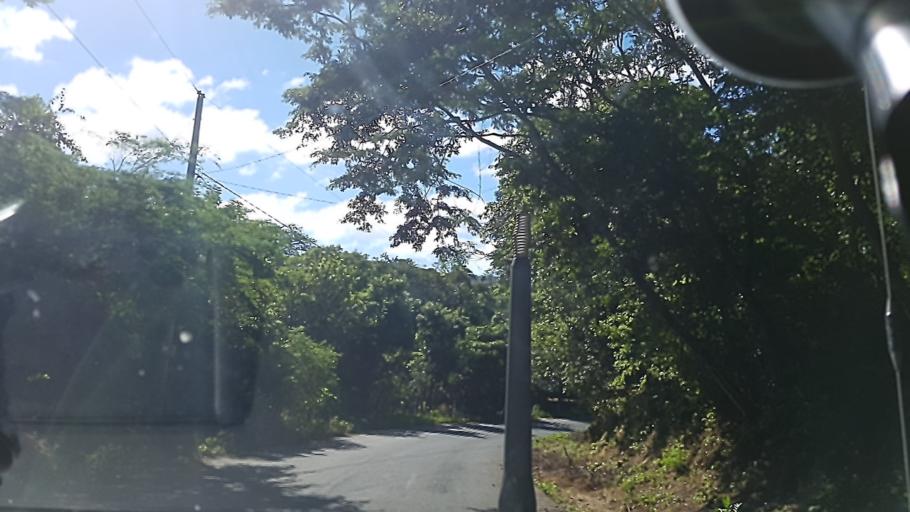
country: NI
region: Carazo
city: Santa Teresa
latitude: 11.6494
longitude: -86.1851
